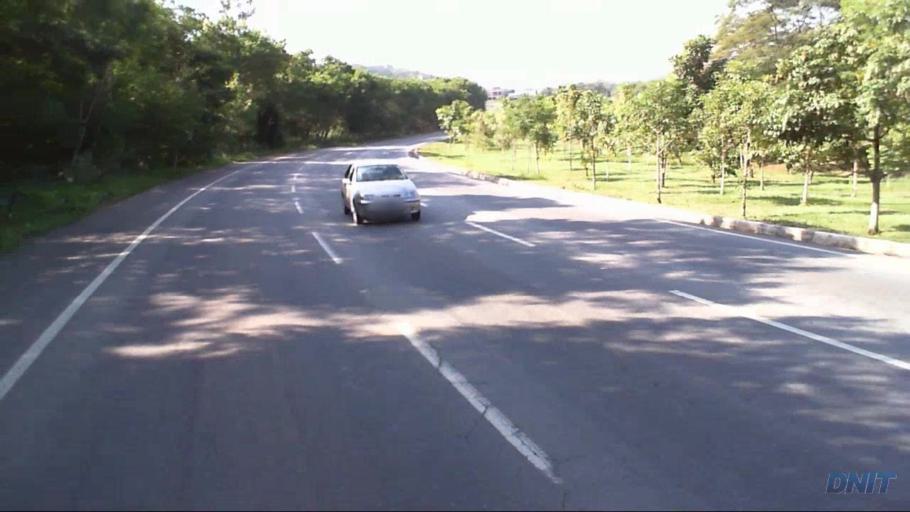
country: BR
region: Minas Gerais
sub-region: Coronel Fabriciano
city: Coronel Fabriciano
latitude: -19.5132
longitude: -42.5762
